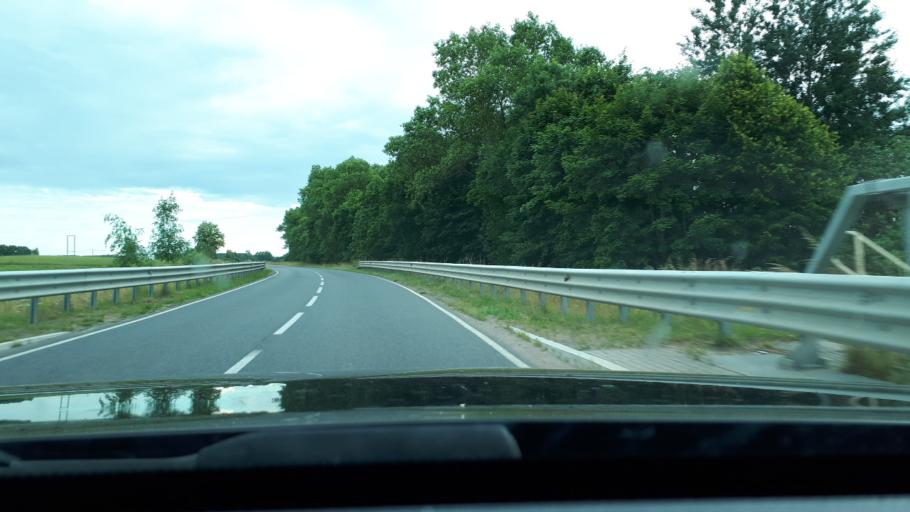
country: PL
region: Warmian-Masurian Voivodeship
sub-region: Powiat olsztynski
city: Olsztynek
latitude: 53.5655
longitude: 20.2664
